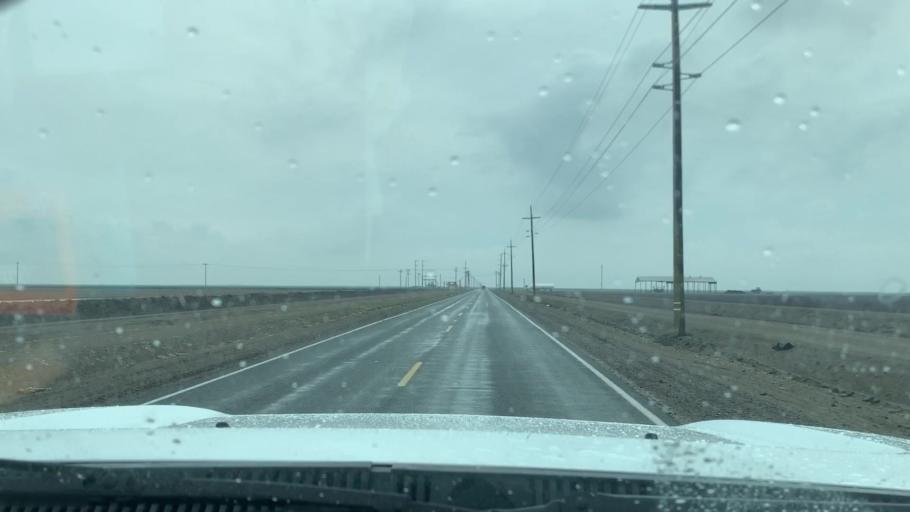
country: US
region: California
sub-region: Kings County
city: Corcoran
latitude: 35.9962
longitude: -119.5720
